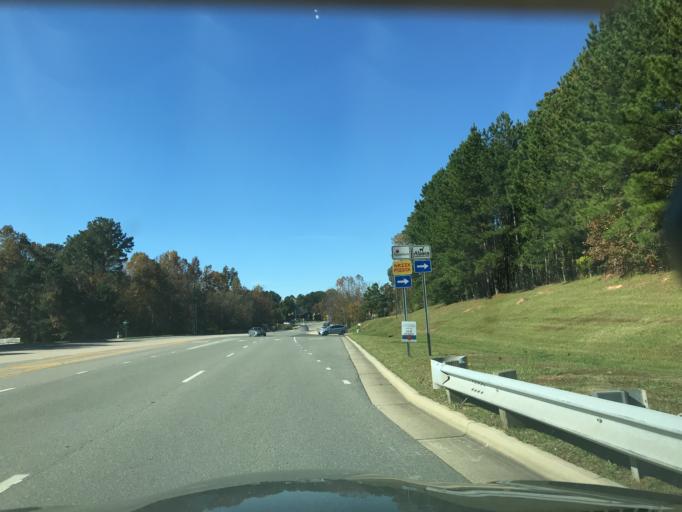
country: US
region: North Carolina
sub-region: Wake County
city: Morrisville
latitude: 35.9000
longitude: -78.7876
